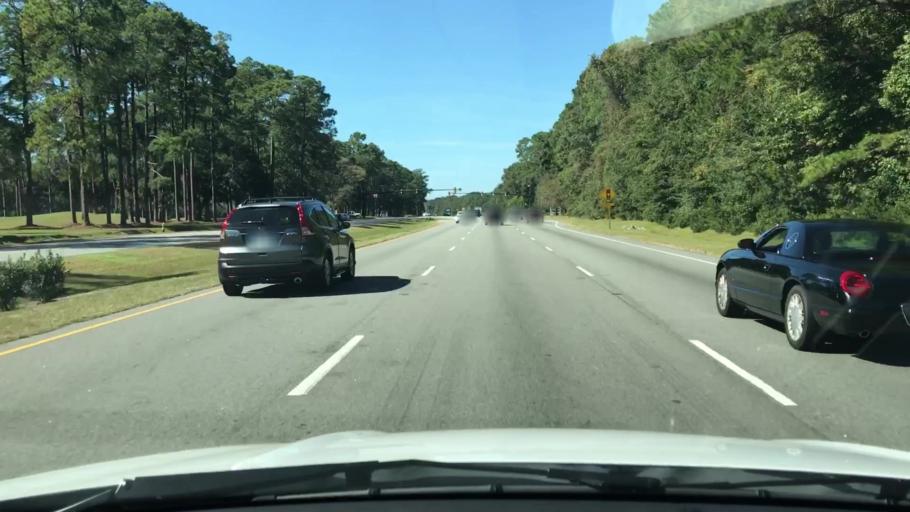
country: US
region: South Carolina
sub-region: Beaufort County
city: Bluffton
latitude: 32.2830
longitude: -80.8799
